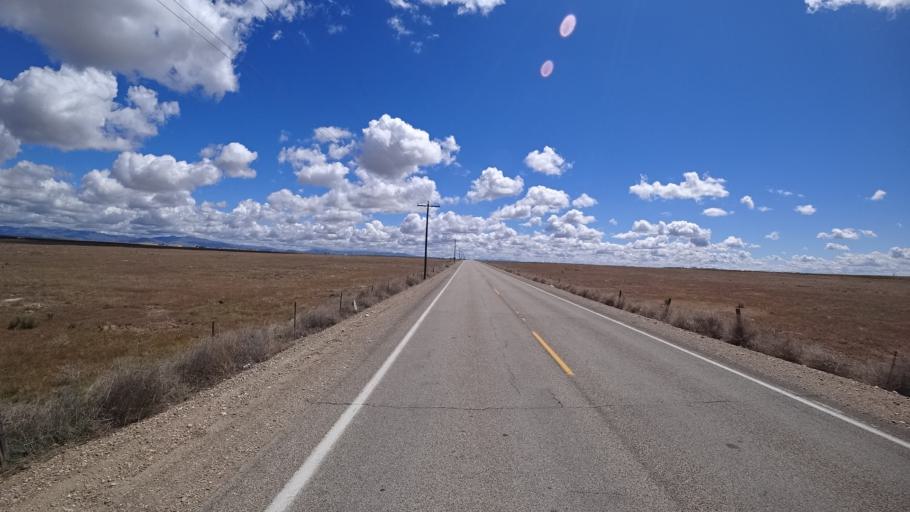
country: US
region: Idaho
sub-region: Ada County
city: Kuna
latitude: 43.4592
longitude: -116.2920
